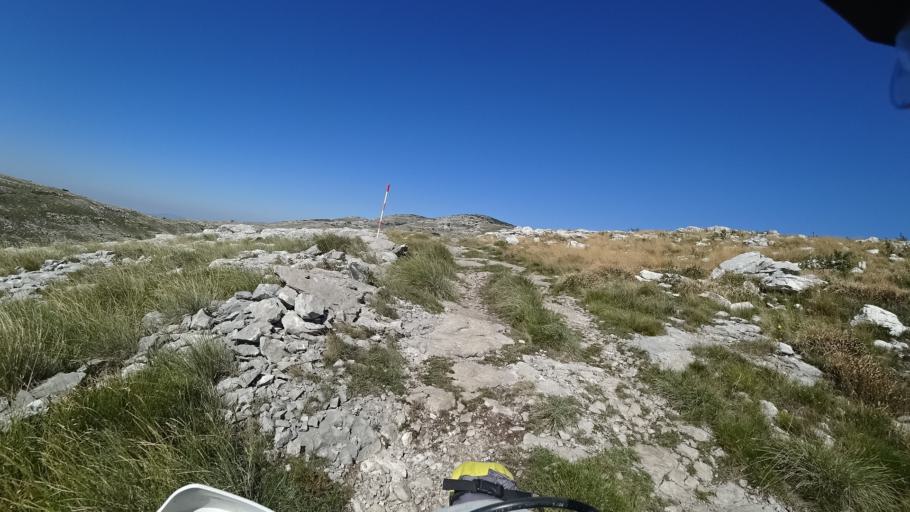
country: HR
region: Splitsko-Dalmatinska
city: Hrvace
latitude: 43.9250
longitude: 16.6068
